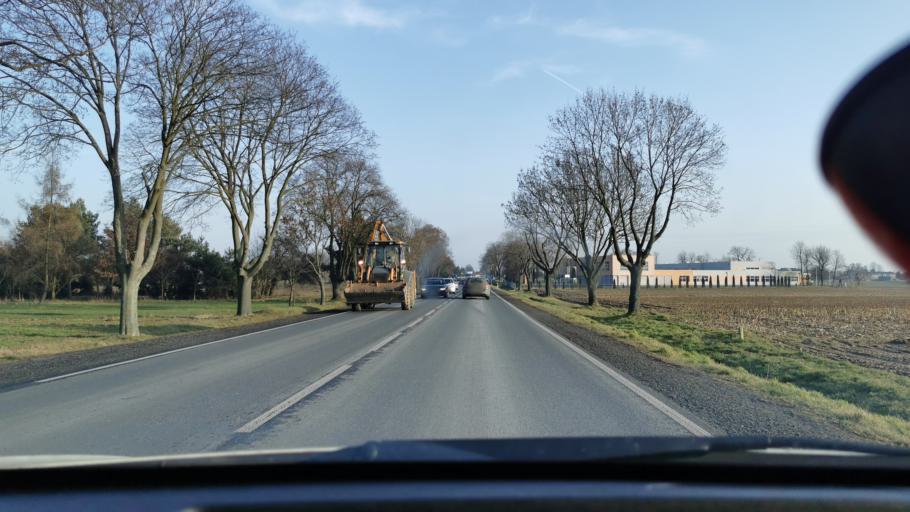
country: PL
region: Lodz Voivodeship
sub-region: Powiat sieradzki
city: Wroblew
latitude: 51.6326
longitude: 18.5427
